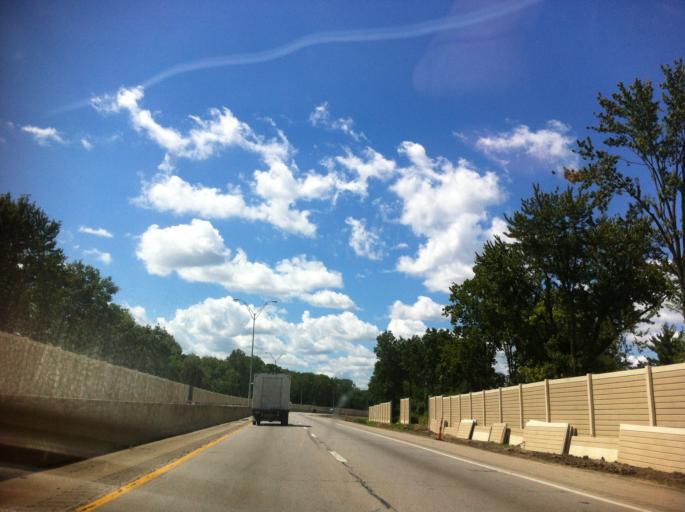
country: US
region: Ohio
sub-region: Lucas County
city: Ottawa Hills
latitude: 41.6880
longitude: -83.6508
